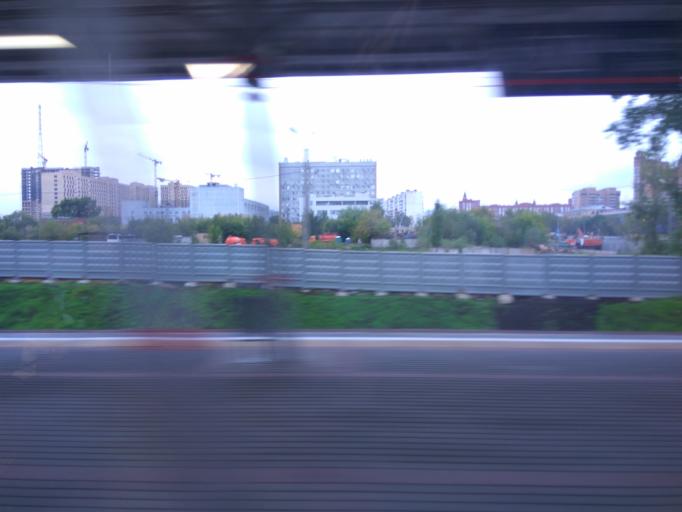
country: RU
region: Moscow
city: Sokol
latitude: 55.7881
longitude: 37.5044
